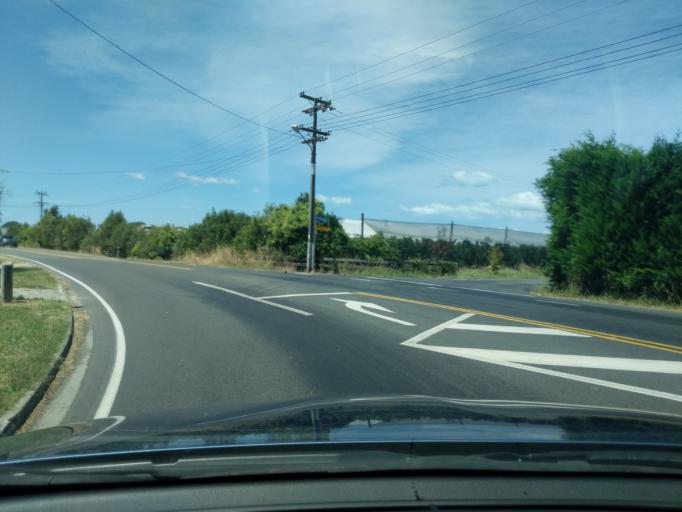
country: NZ
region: Tasman
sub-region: Tasman District
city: Motueka
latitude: -41.0697
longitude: 172.9850
